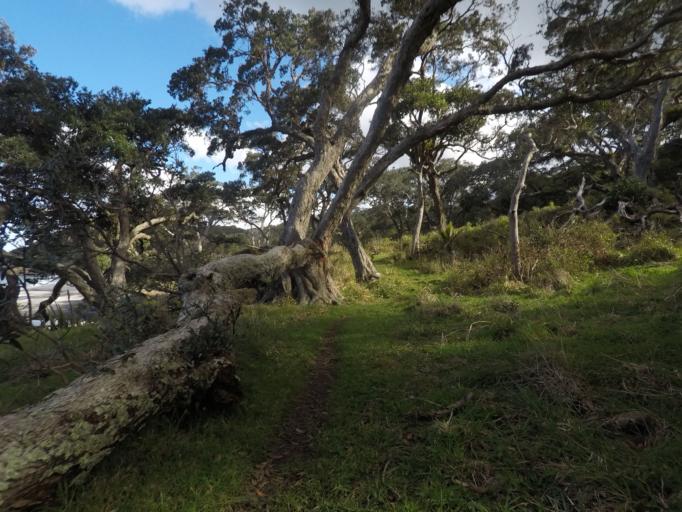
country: NZ
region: Bay of Plenty
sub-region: Western Bay of Plenty District
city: Waihi Beach
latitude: -37.3823
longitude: 175.9372
